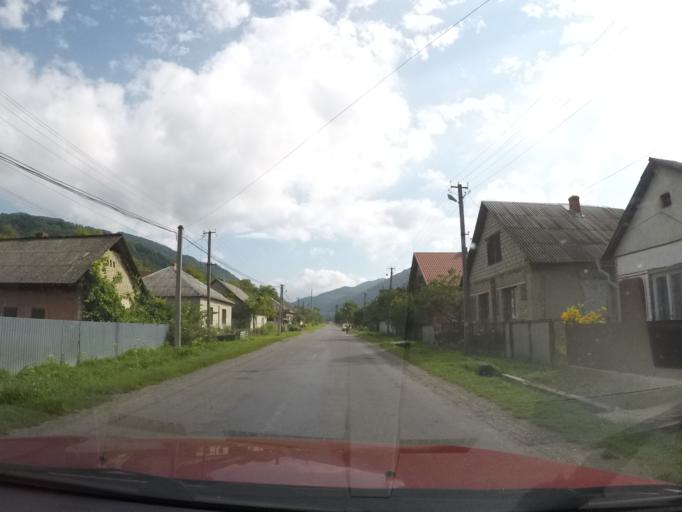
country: UA
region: Zakarpattia
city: Velykyi Bereznyi
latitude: 48.9447
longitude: 22.5983
